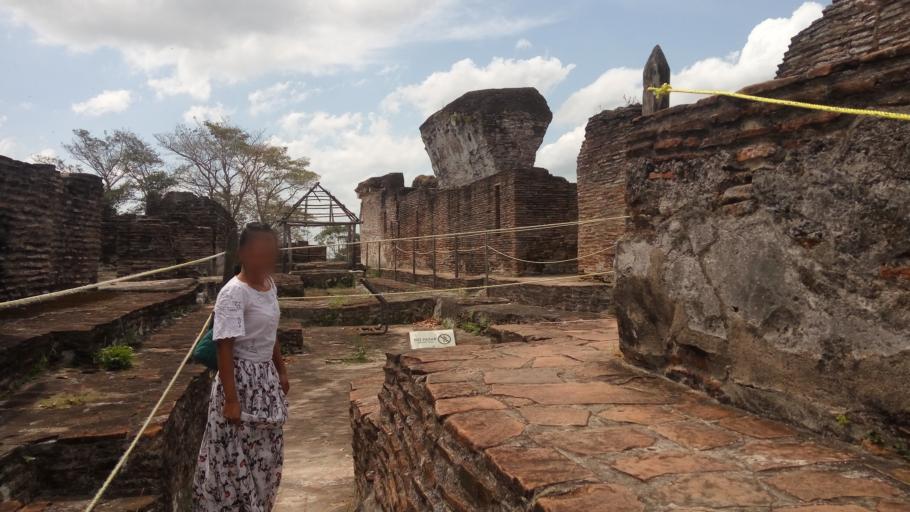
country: MX
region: Tabasco
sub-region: Comalcalco
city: Oriente 1ra. Seccion (Santo Domingo)
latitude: 18.2784
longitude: -93.2002
